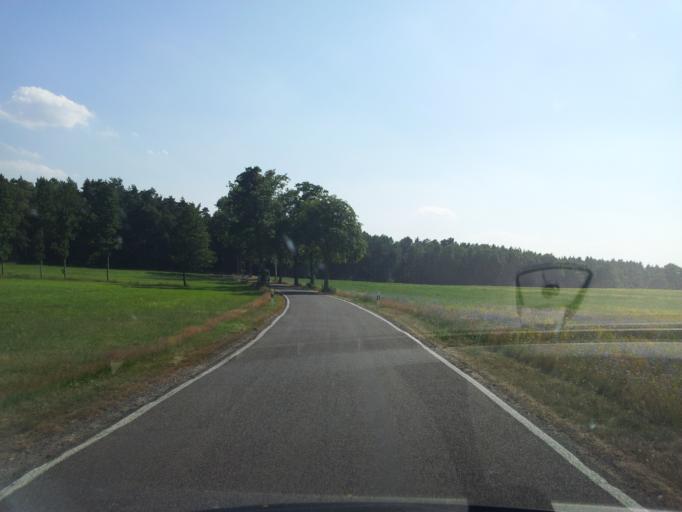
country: DE
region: Saxony
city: Hockendorf
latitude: 51.2129
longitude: 13.9042
